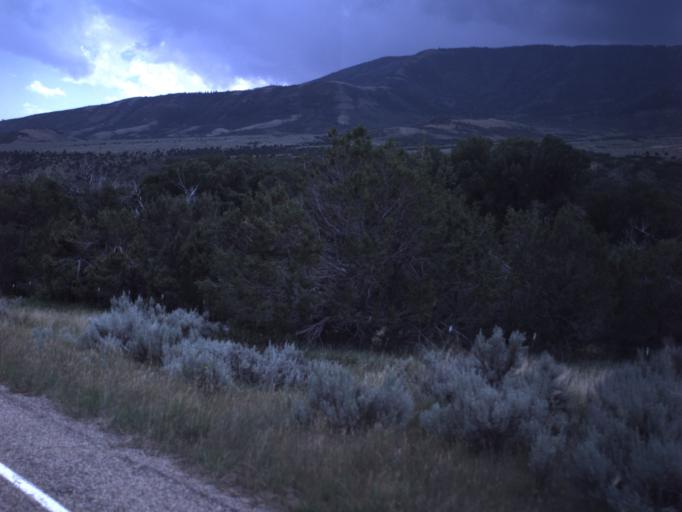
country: US
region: Utah
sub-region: Duchesne County
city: Duchesne
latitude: 40.4118
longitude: -110.7779
